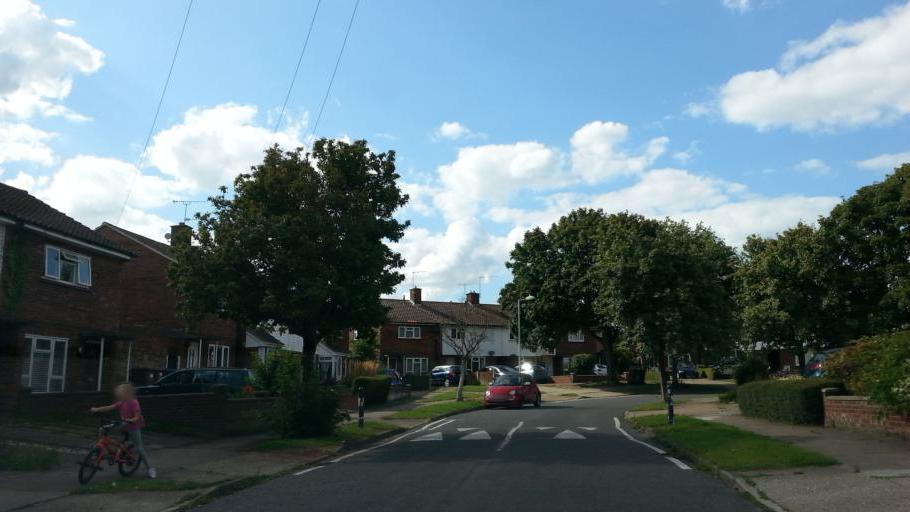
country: GB
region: England
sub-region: Suffolk
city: Bury St Edmunds
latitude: 52.2619
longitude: 0.6966
